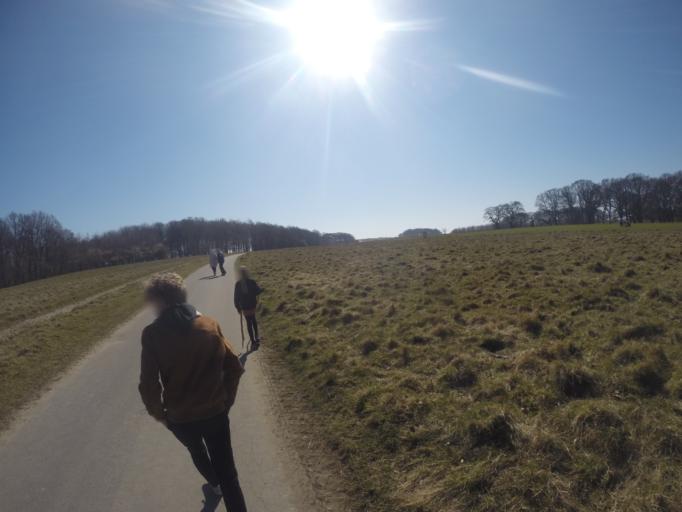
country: DK
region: Capital Region
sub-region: Rudersdal Kommune
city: Trorod
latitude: 55.7997
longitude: 12.5721
